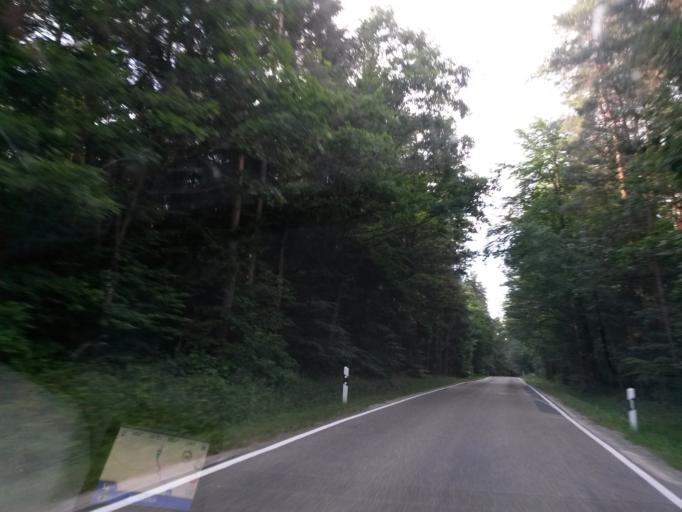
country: DE
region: Bavaria
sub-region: Regierungsbezirk Mittelfranken
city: Markt Taschendorf
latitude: 49.6859
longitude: 10.5755
